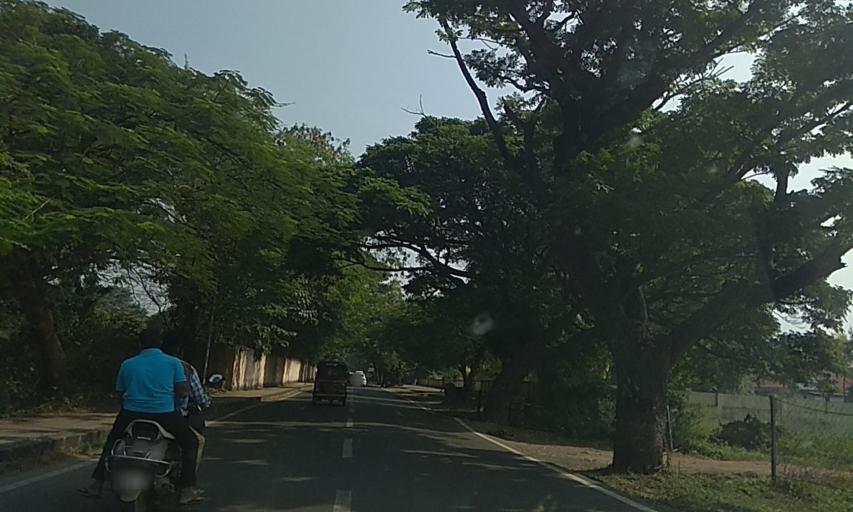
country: IN
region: Maharashtra
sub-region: Pune Division
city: Khadki
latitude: 18.5574
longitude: 73.8489
